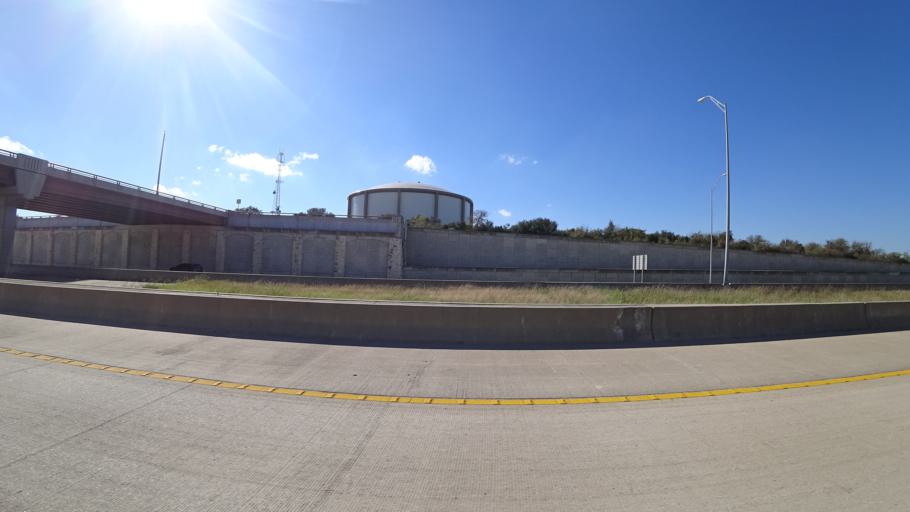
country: US
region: Texas
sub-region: Travis County
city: Wells Branch
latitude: 30.4608
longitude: -97.6992
